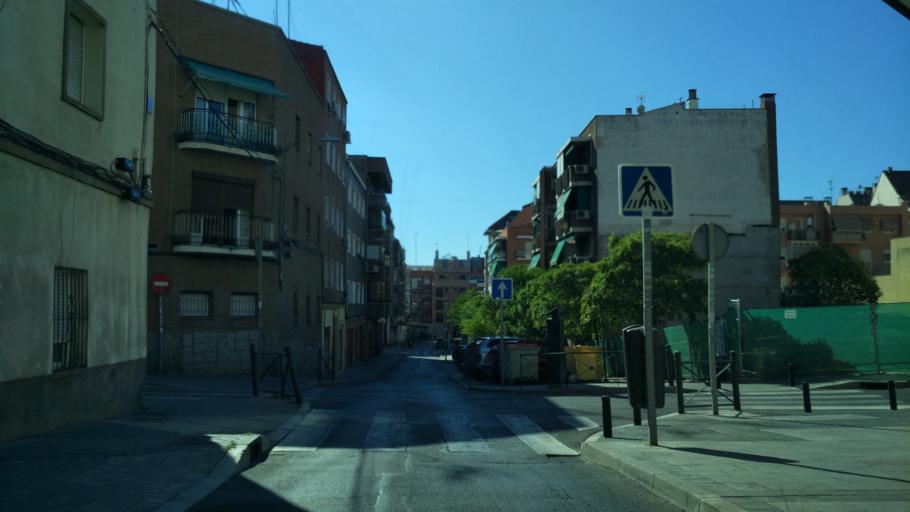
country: ES
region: Madrid
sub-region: Provincia de Madrid
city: Tetuan de las Victorias
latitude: 40.4658
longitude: -3.6968
